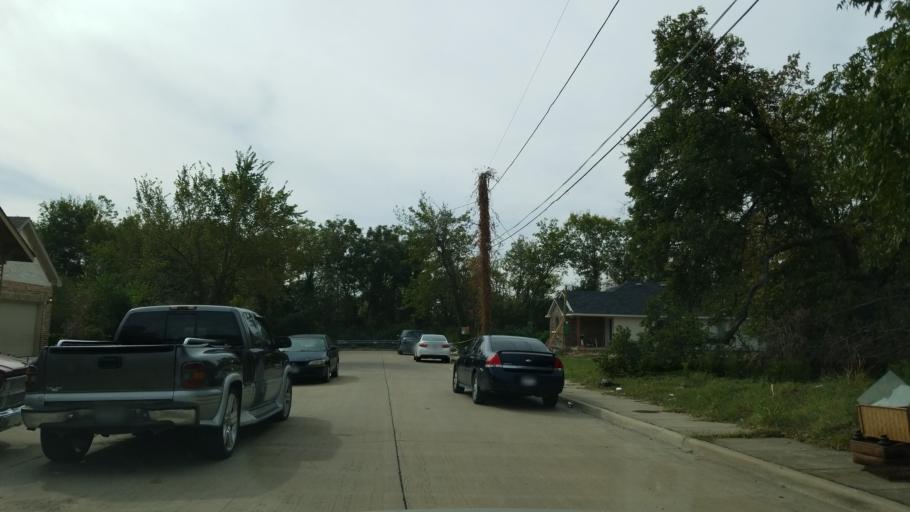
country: US
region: Texas
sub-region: Dallas County
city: Dallas
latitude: 32.7795
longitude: -96.7395
